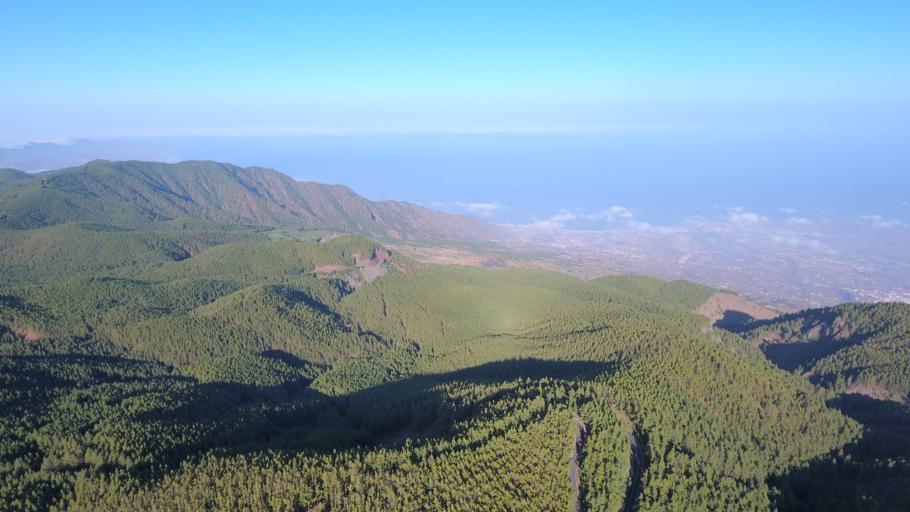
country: ES
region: Canary Islands
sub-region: Provincia de Santa Cruz de Tenerife
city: Arafo
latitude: 28.3739
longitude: -16.4632
